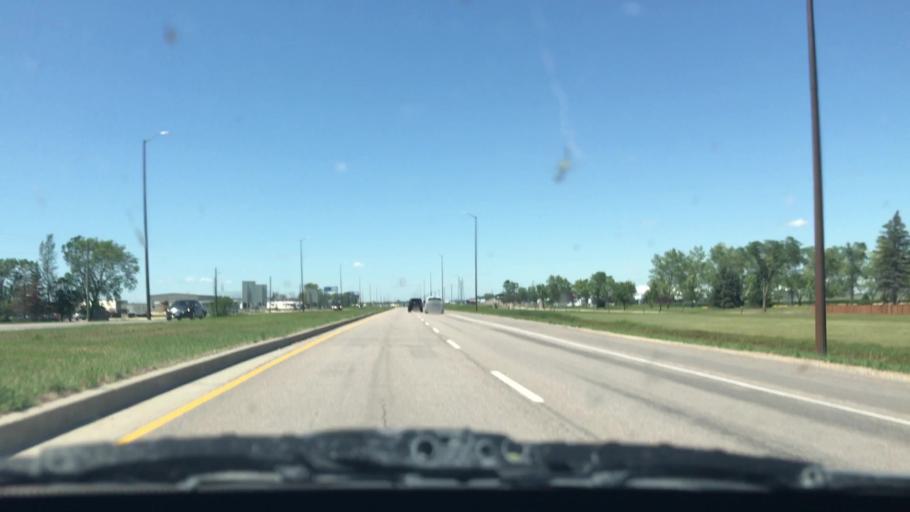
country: CA
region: Manitoba
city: Winnipeg
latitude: 49.8429
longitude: -96.9907
